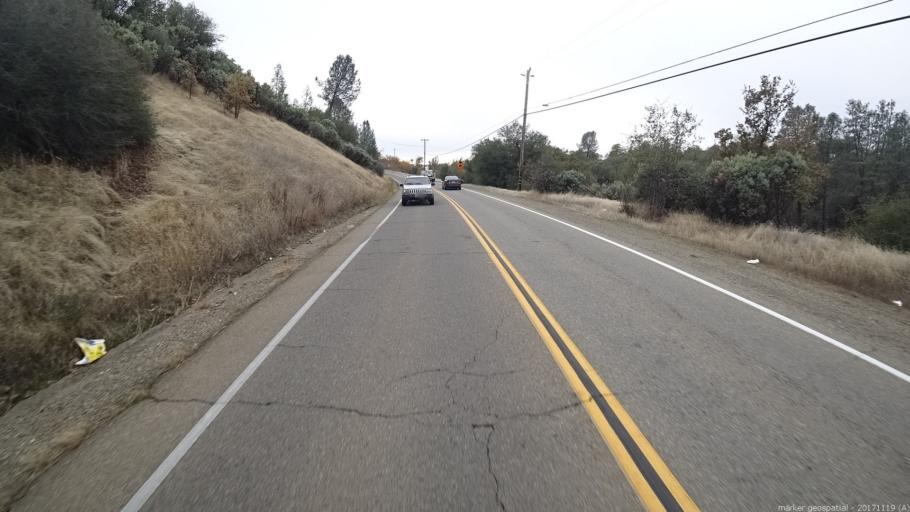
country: US
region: California
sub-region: Shasta County
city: Redding
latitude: 40.4834
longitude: -122.3971
